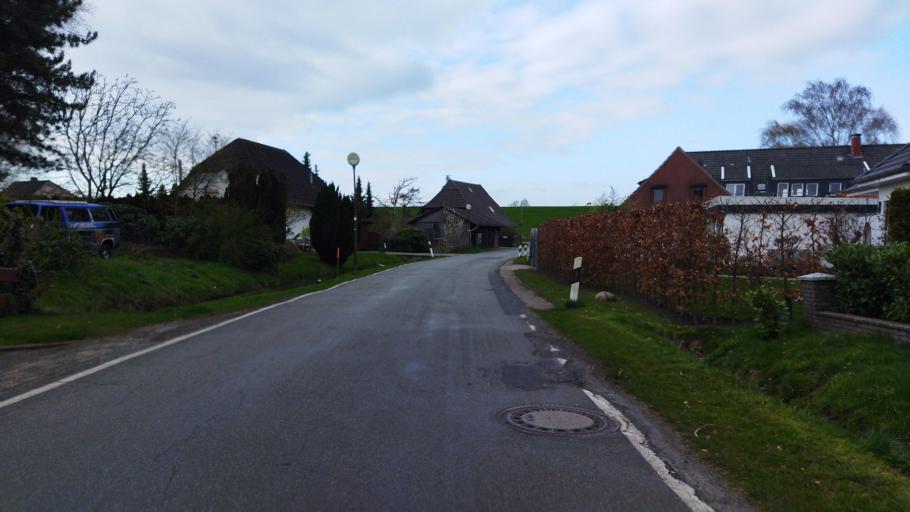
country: DE
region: Lower Saxony
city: Lemwerder
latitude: 53.1662
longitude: 8.5816
